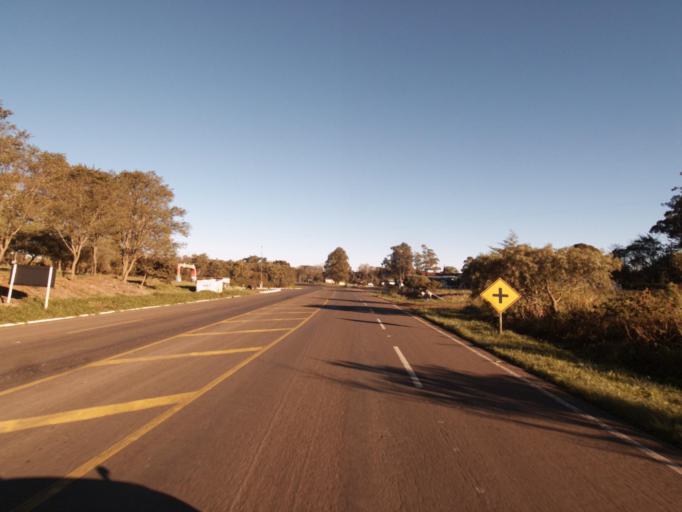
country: BR
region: Rio Grande do Sul
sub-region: Frederico Westphalen
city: Frederico Westphalen
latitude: -26.7831
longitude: -53.2827
